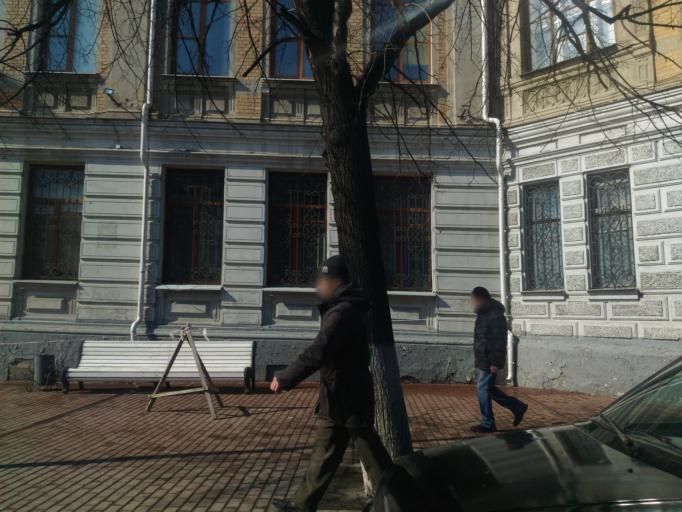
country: RU
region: Ulyanovsk
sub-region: Ulyanovskiy Rayon
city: Ulyanovsk
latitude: 54.3122
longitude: 48.3957
